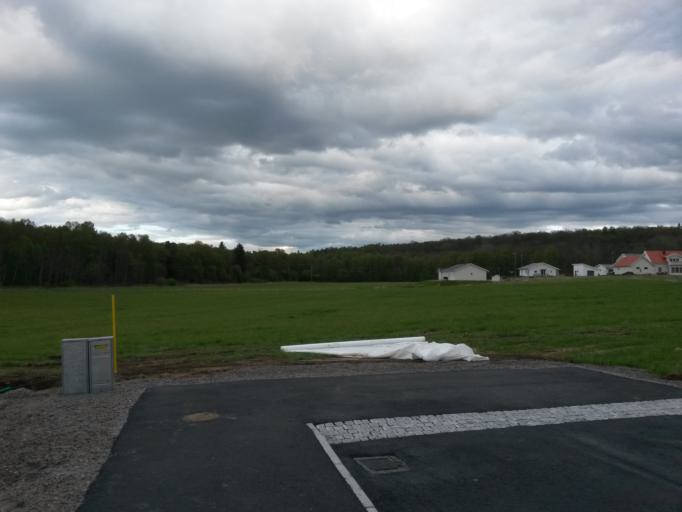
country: SE
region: Vaestra Goetaland
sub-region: Vargarda Kommun
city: Vargarda
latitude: 58.0216
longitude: 12.8166
